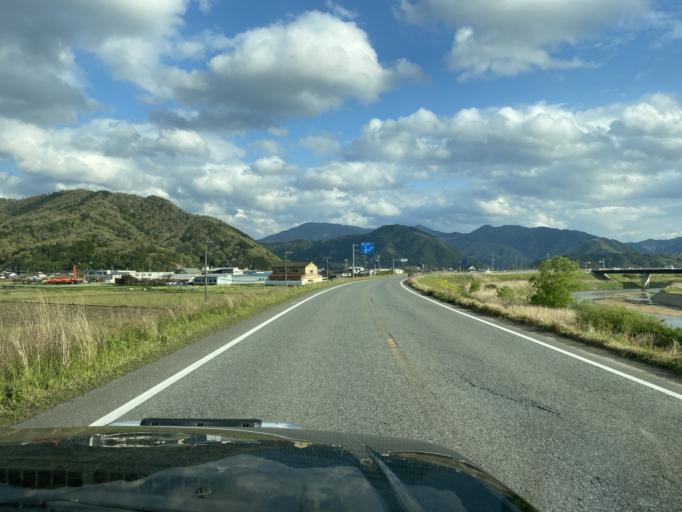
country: JP
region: Hyogo
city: Toyooka
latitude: 35.4837
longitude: 134.8610
